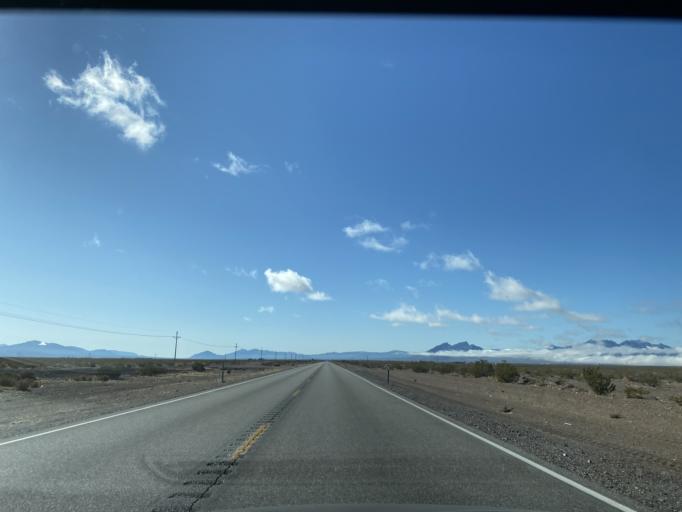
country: US
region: Nevada
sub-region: Nye County
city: Beatty
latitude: 36.5519
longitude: -116.4166
